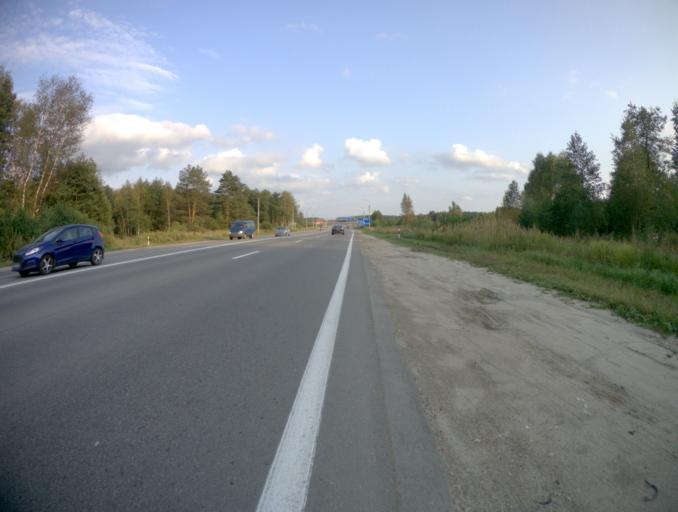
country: RU
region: Vladimir
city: Kommunar
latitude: 56.0843
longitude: 40.4637
